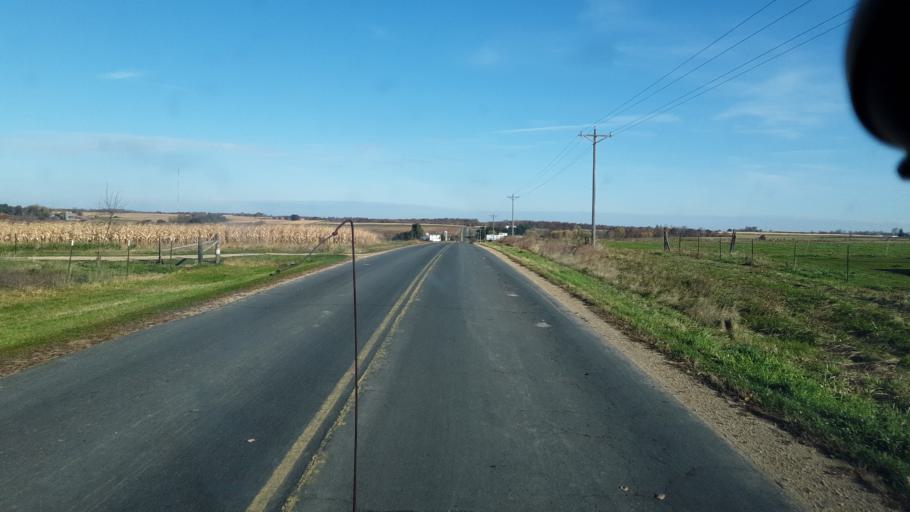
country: US
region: Wisconsin
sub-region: Vernon County
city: Hillsboro
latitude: 43.7610
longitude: -90.4331
